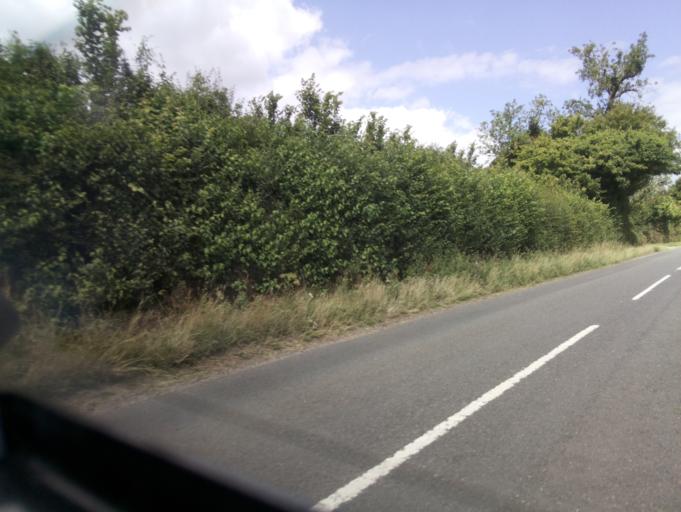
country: GB
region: England
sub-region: Buckinghamshire
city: Winslow
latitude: 51.9319
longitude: -0.8354
